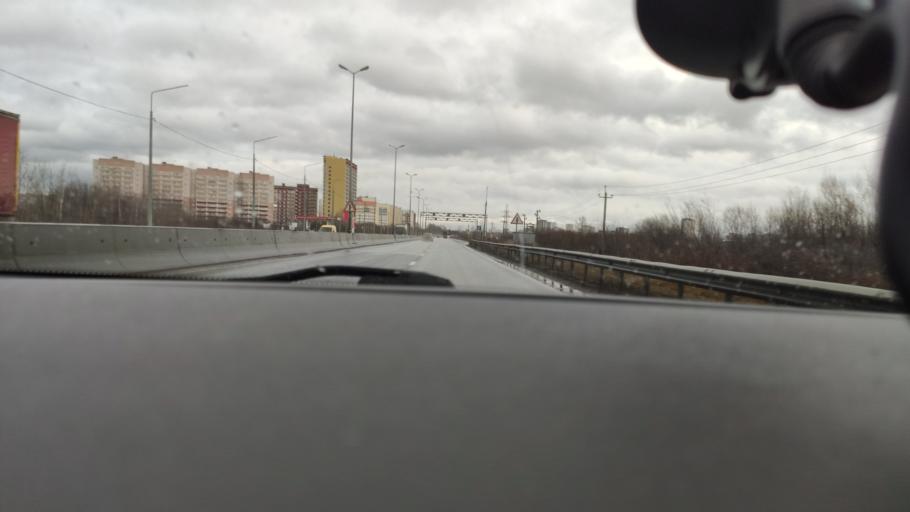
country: RU
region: Perm
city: Kondratovo
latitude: 57.9996
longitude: 56.0986
